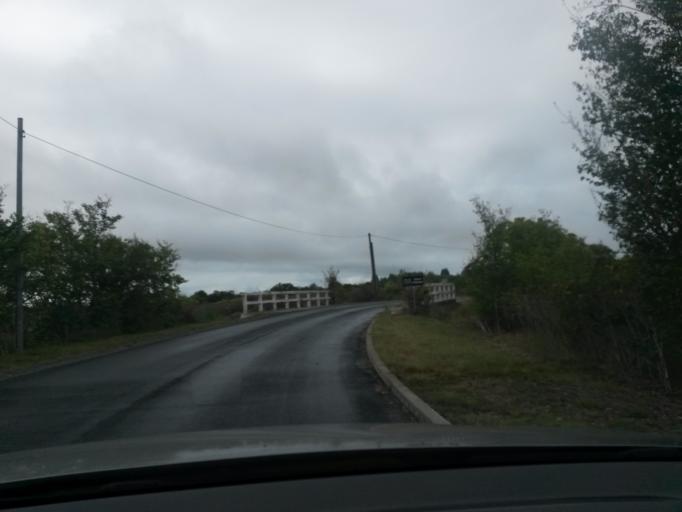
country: FR
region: Poitou-Charentes
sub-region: Departement de la Charente-Maritime
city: Saint-Trojan-les-Bains
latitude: 45.8759
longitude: -1.2018
